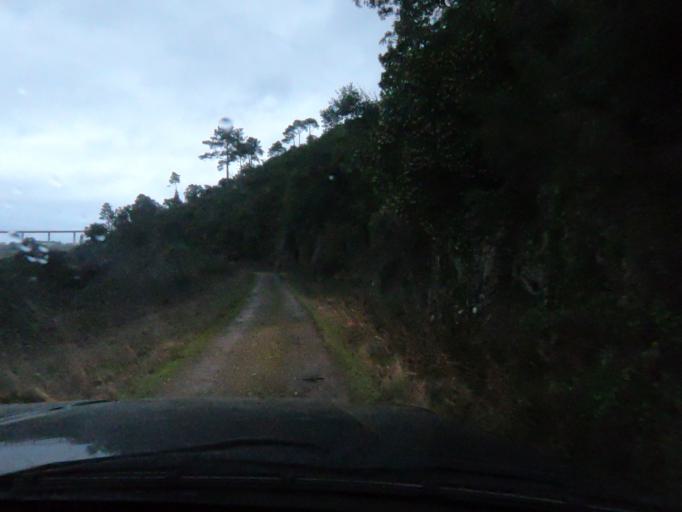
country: PT
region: Vila Real
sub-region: Vila Real
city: Vila Real
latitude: 41.2637
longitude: -7.7439
